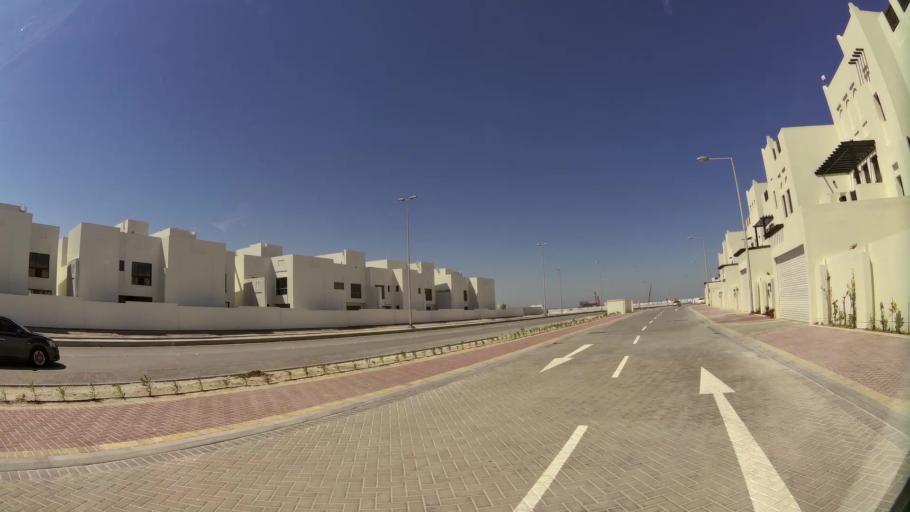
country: BH
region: Muharraq
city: Al Muharraq
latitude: 26.3014
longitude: 50.6361
